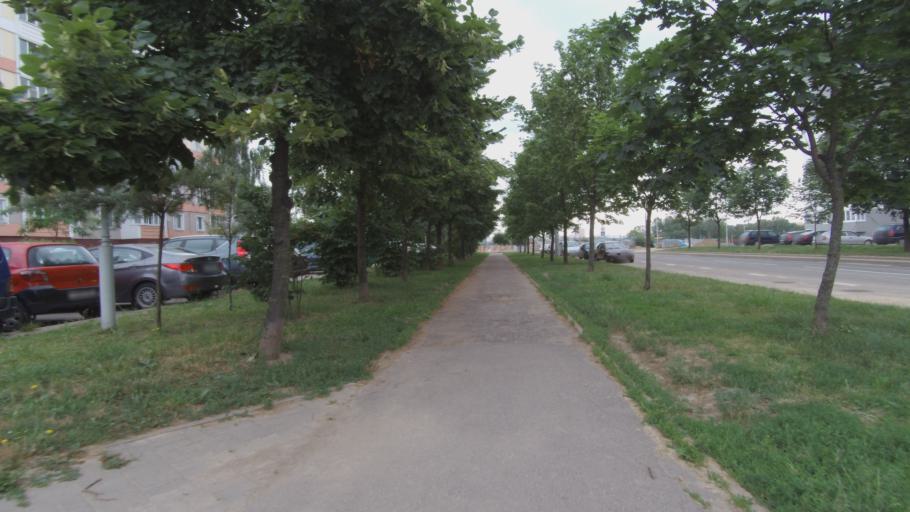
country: BY
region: Minsk
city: Syenitsa
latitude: 53.8487
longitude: 27.5637
